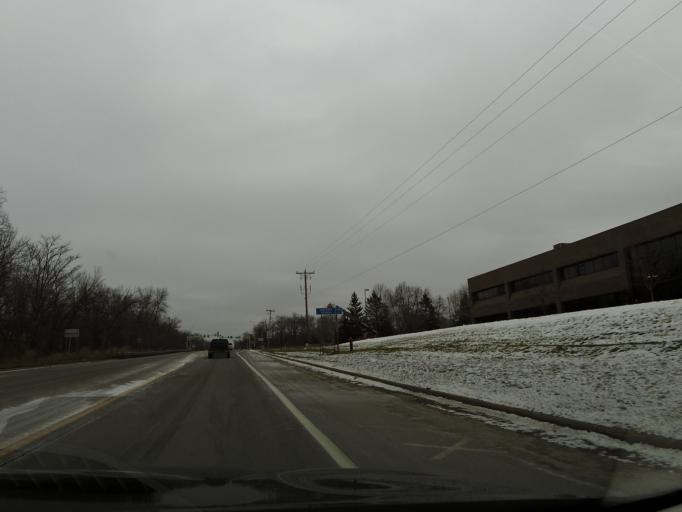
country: US
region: Minnesota
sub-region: Hennepin County
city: Maple Plain
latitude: 45.0101
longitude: -93.6685
